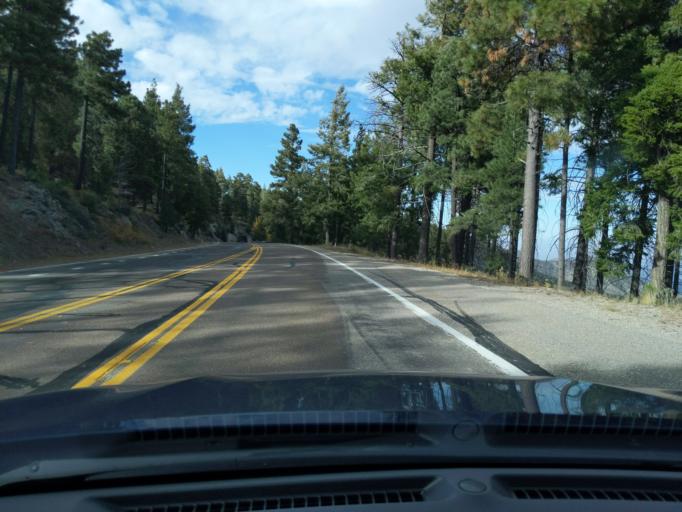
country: US
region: Arizona
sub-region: Pinal County
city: Oracle
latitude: 32.4408
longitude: -110.7525
